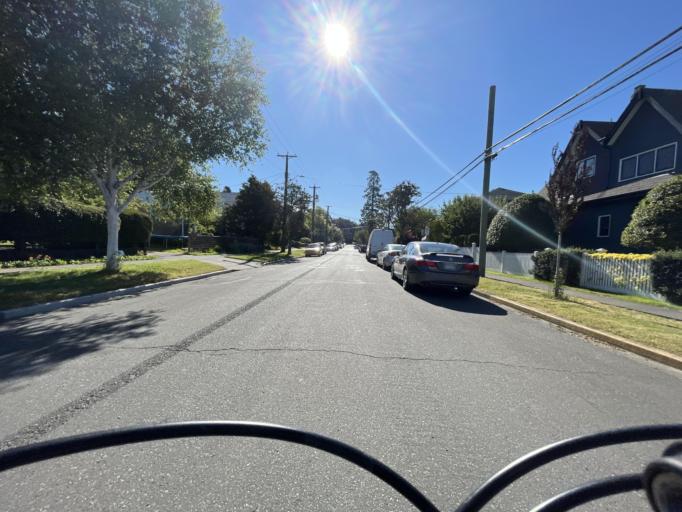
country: CA
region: British Columbia
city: Victoria
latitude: 48.4191
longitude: -123.3500
